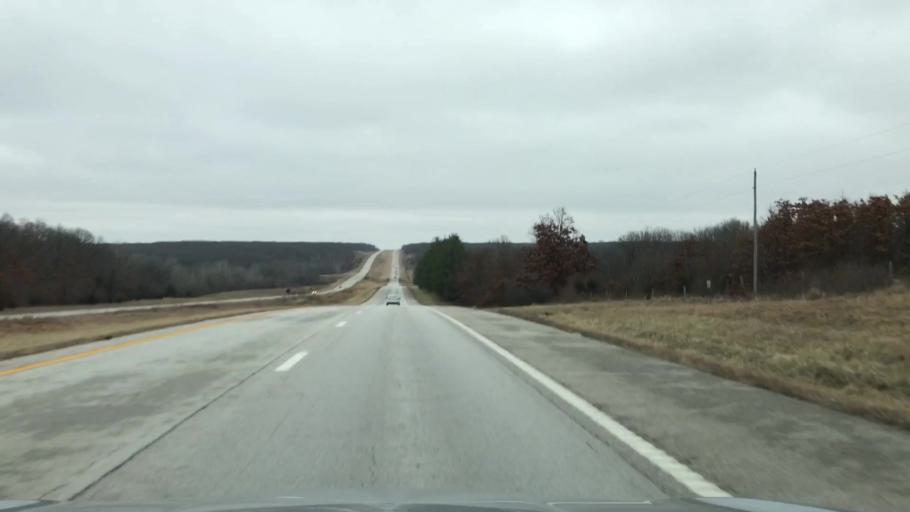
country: US
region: Missouri
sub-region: Linn County
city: Marceline
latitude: 39.7590
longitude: -92.8662
